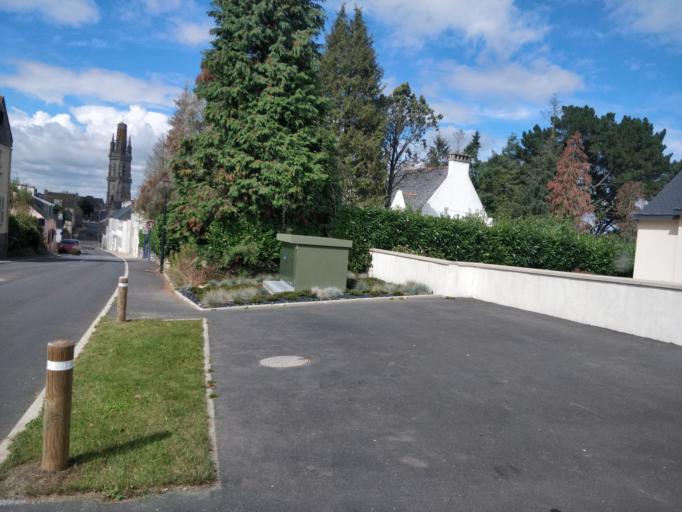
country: FR
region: Brittany
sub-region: Departement du Finistere
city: Lampaul-Guimiliau
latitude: 48.4922
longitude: -4.0370
